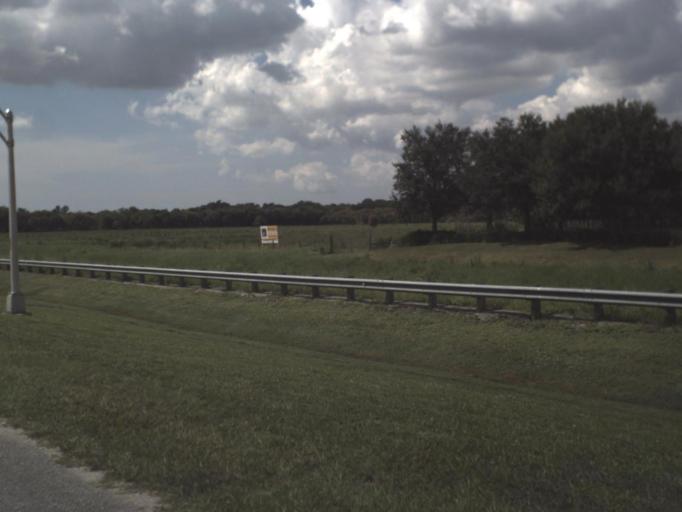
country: US
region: Florida
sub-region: Sarasota County
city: Fruitville
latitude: 27.3383
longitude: -82.4538
